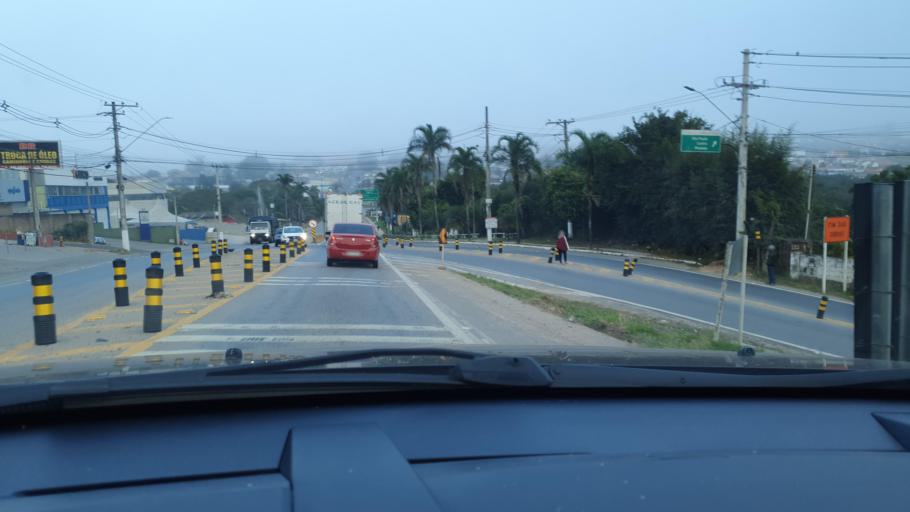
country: BR
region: Sao Paulo
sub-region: Ibiuna
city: Ibiuna
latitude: -23.6567
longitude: -47.2077
